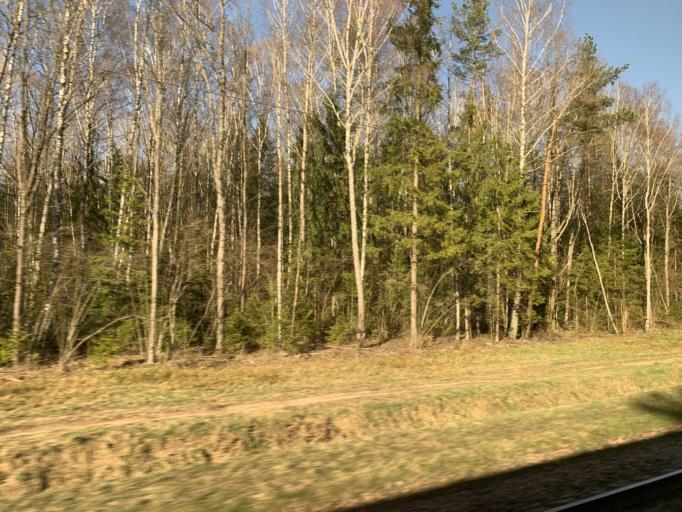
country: BY
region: Grodnenskaya
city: Smarhon'
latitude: 54.4857
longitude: 26.3182
